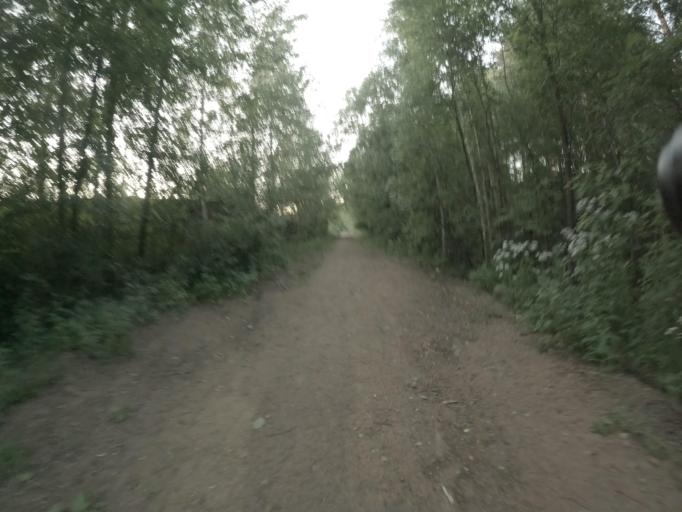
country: RU
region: St.-Petersburg
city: Krasnogvargeisky
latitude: 59.9883
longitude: 30.5316
